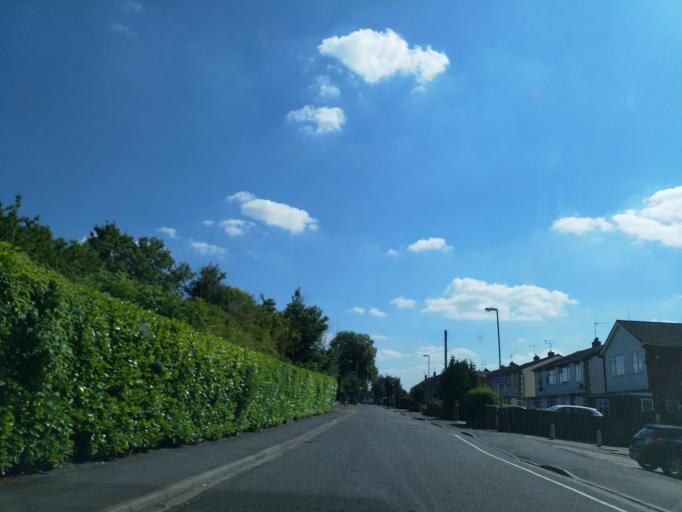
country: GB
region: England
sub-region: Warwickshire
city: Kenilworth
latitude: 52.3432
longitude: -1.5714
